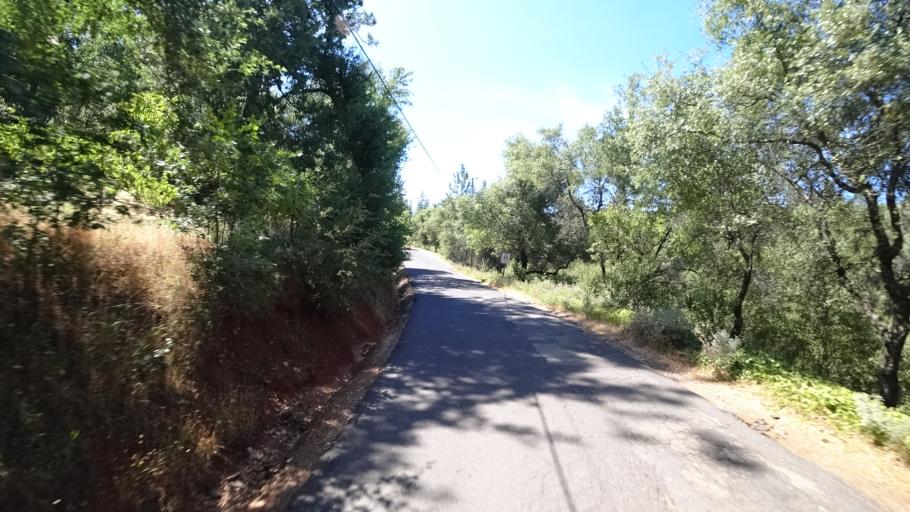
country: US
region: California
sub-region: Calaveras County
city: Murphys
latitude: 38.1439
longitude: -120.4692
